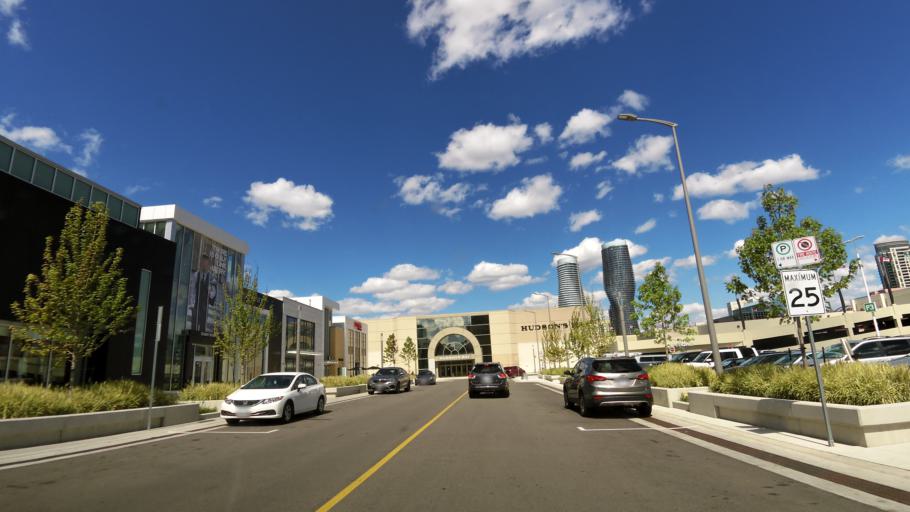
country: CA
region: Ontario
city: Mississauga
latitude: 43.5912
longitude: -79.6420
